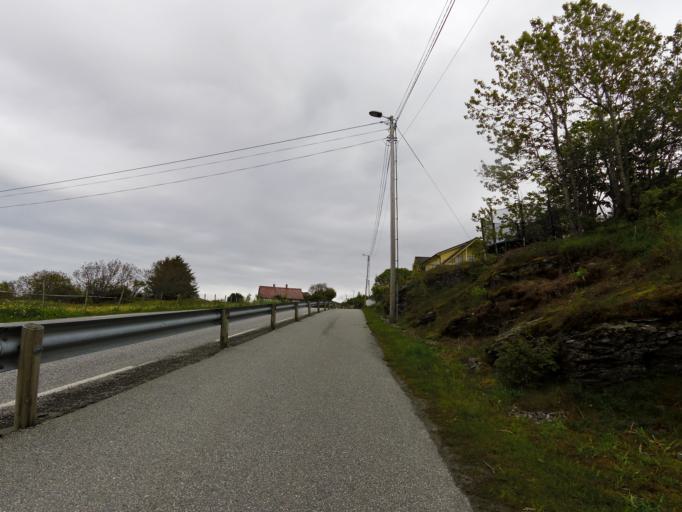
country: NO
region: Hordaland
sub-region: Sveio
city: Sveio
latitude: 59.6017
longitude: 5.2160
